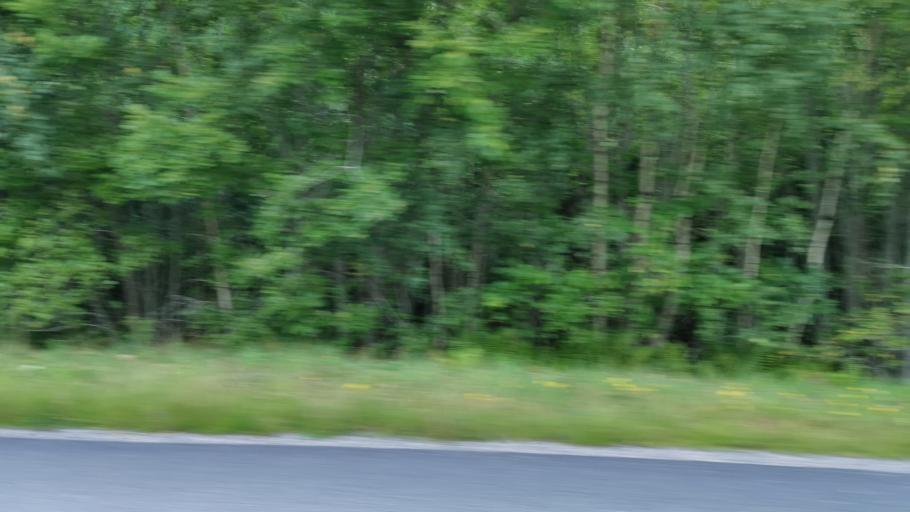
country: SE
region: Vaestra Goetaland
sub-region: Sotenas Kommun
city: Hunnebostrand
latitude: 58.4810
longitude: 11.3913
